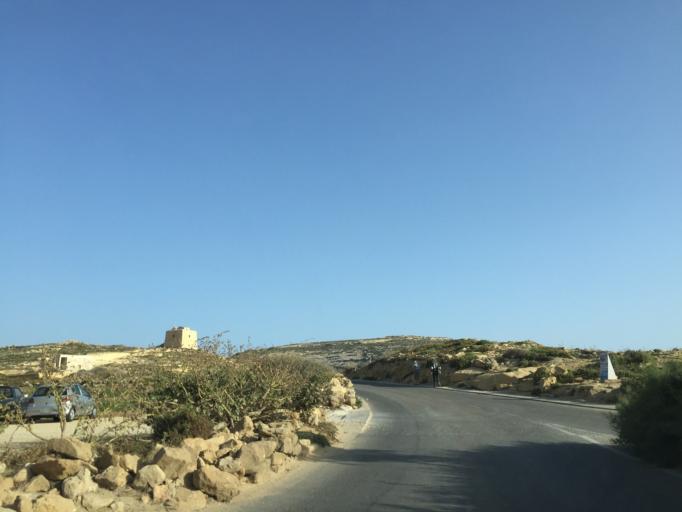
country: MT
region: Saint Lawrence
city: San Lawrenz
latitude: 36.0522
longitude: 14.1904
